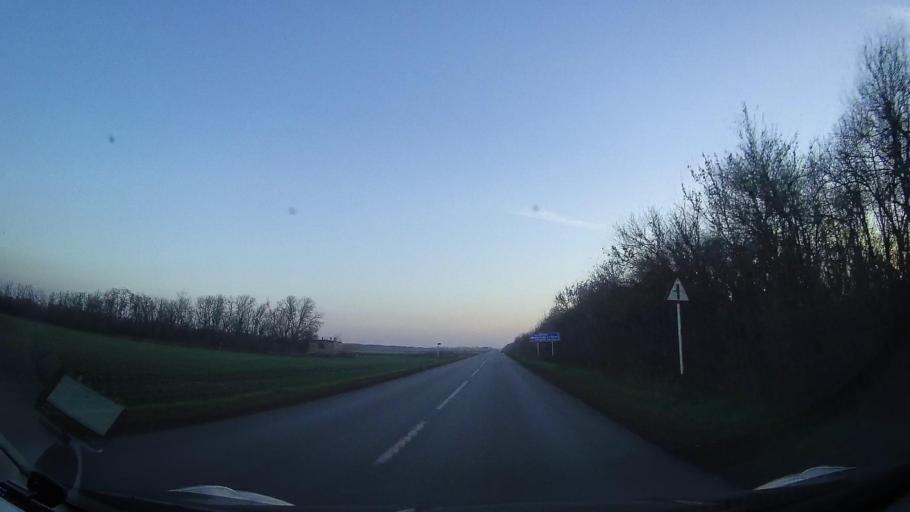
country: RU
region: Rostov
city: Zernograd
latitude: 47.0301
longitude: 40.3917
